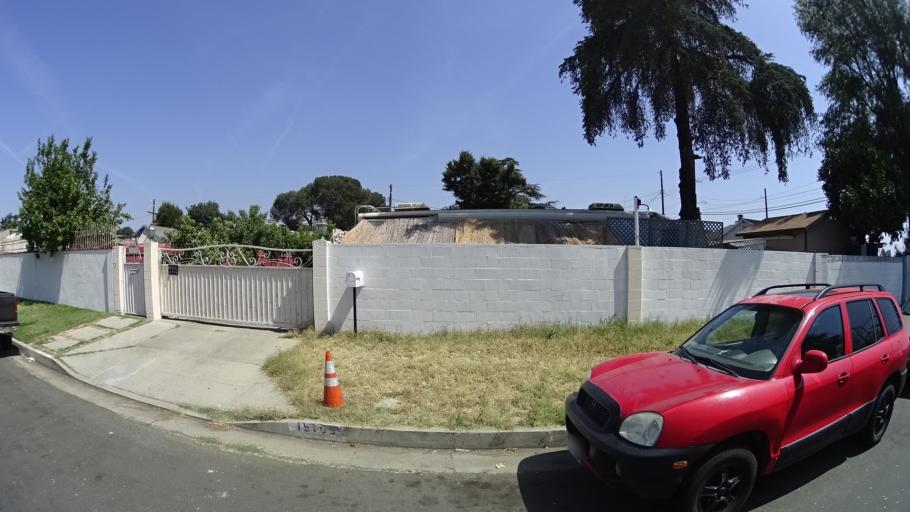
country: US
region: California
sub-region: Los Angeles County
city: Van Nuys
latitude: 34.2066
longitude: -118.4622
